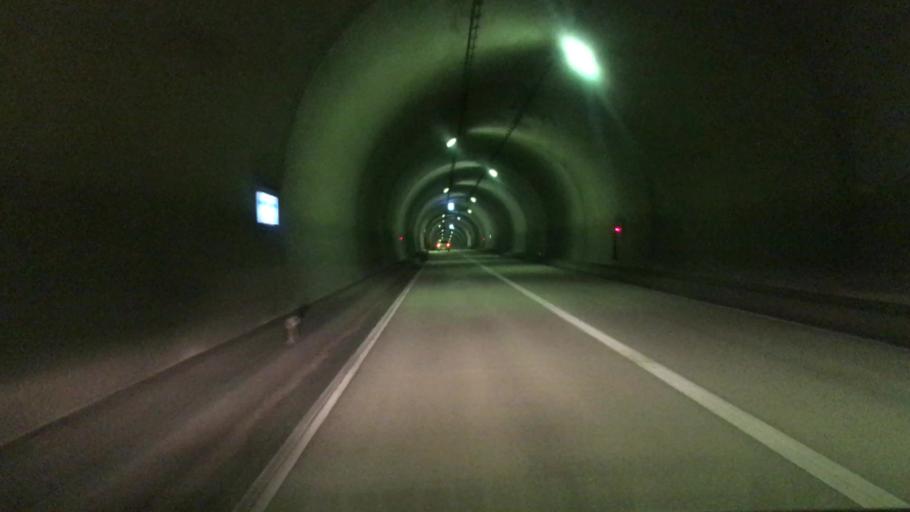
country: JP
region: Hyogo
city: Toyooka
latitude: 35.4175
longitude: 134.7399
